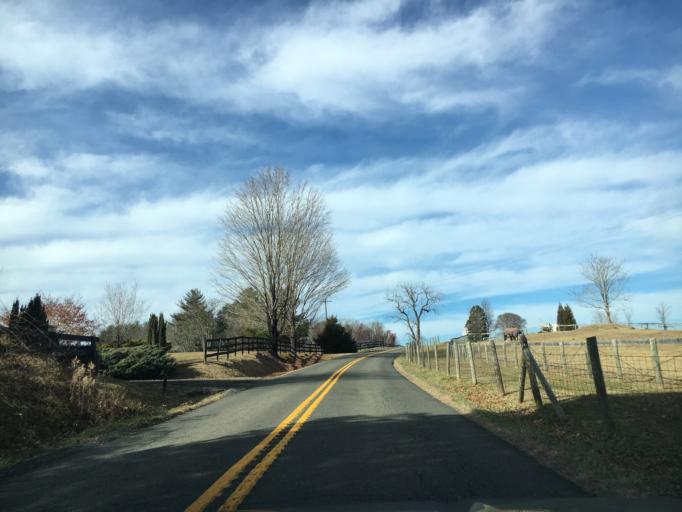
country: US
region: Virginia
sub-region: Fauquier County
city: Marshall
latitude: 38.7843
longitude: -77.9896
